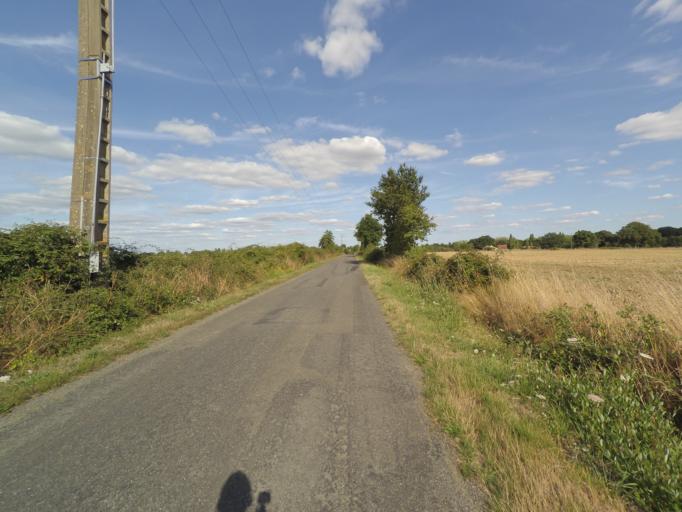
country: FR
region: Pays de la Loire
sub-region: Departement de la Loire-Atlantique
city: Vieillevigne
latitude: 46.9592
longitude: -1.4389
